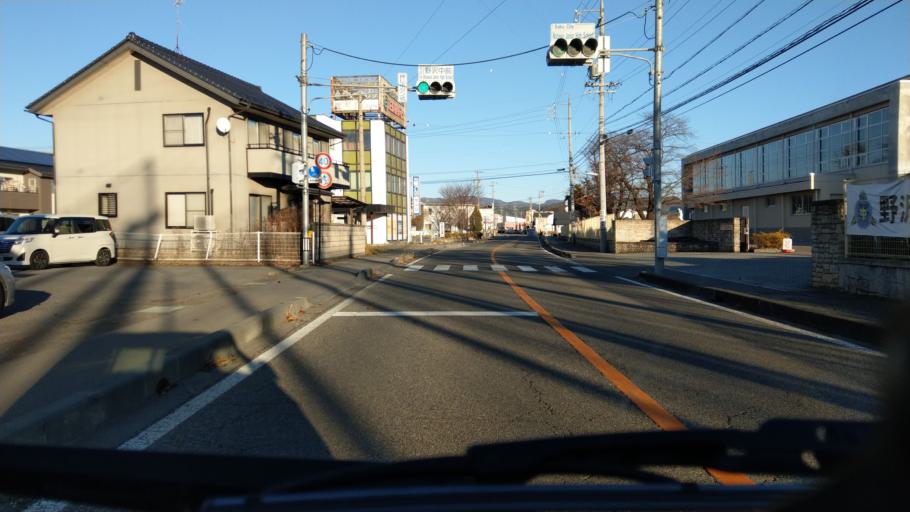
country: JP
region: Nagano
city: Saku
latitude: 36.2252
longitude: 138.4616
